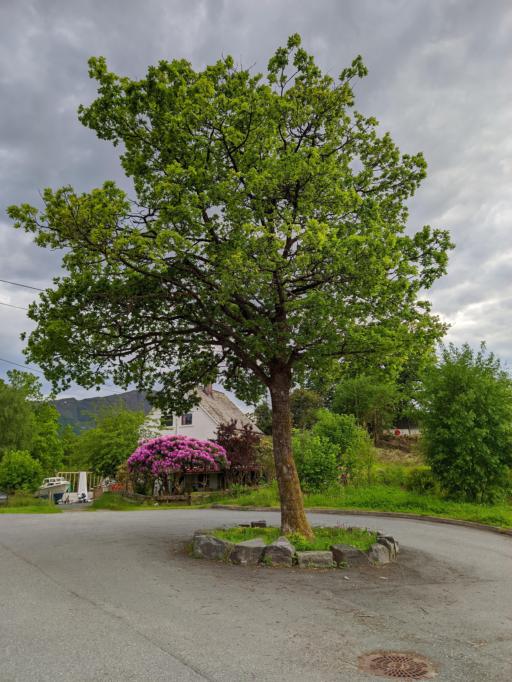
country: NO
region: Hordaland
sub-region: Tysnes
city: Uggdal
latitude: 60.0597
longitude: 5.6425
